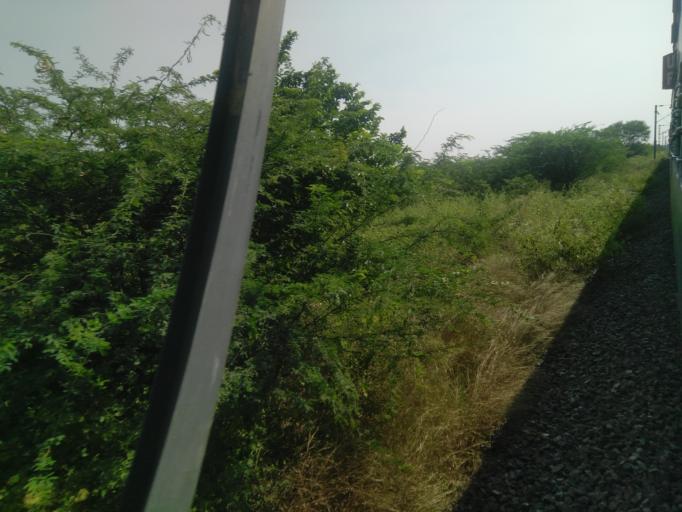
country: IN
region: Tamil Nadu
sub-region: Coimbatore
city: Periyanayakkanpalaiyam
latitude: 11.1237
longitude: 76.9486
